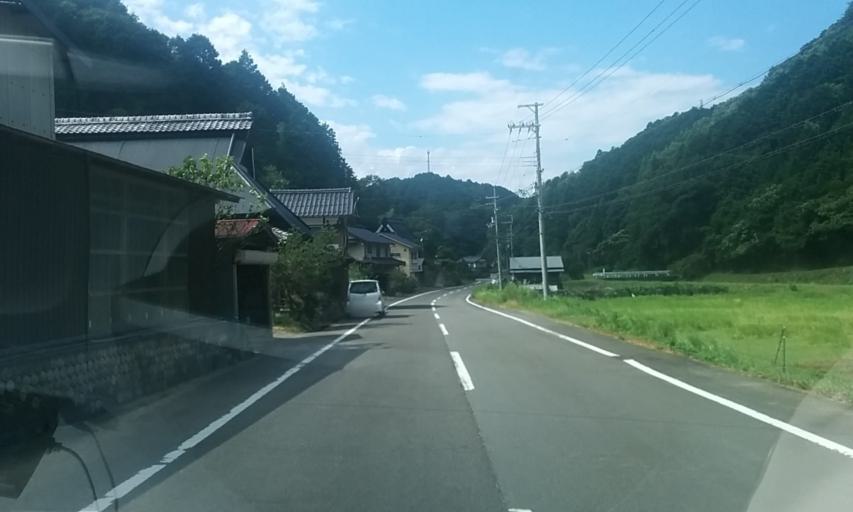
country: JP
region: Kyoto
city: Fukuchiyama
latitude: 35.3690
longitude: 135.1606
